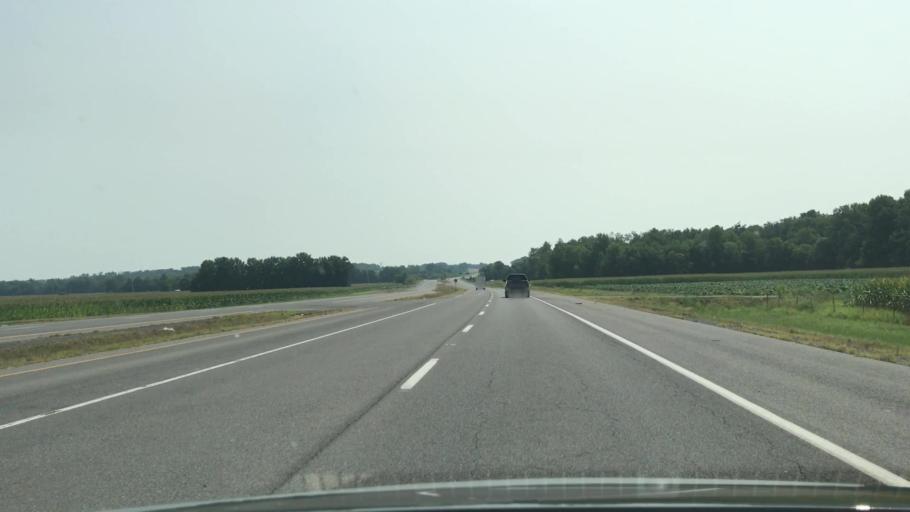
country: US
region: Kentucky
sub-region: Calloway County
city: Murray
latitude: 36.6516
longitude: -88.2971
